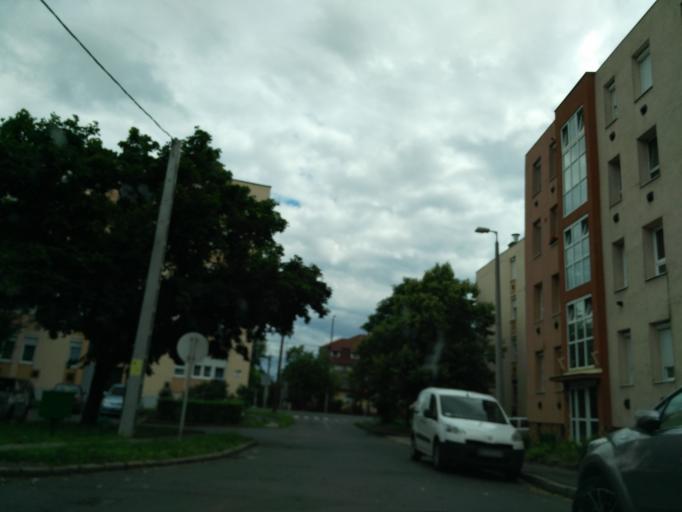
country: HU
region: Hajdu-Bihar
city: Debrecen
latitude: 47.5478
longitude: 21.6445
